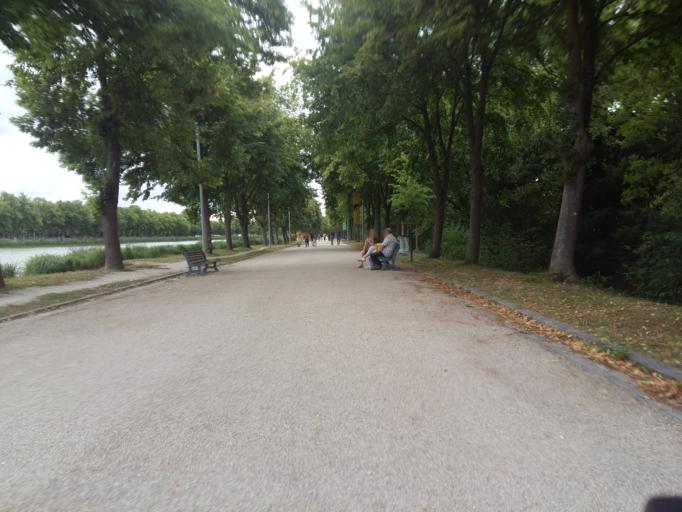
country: FR
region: Picardie
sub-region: Departement de la Somme
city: Amiens
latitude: 49.8995
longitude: 2.2802
